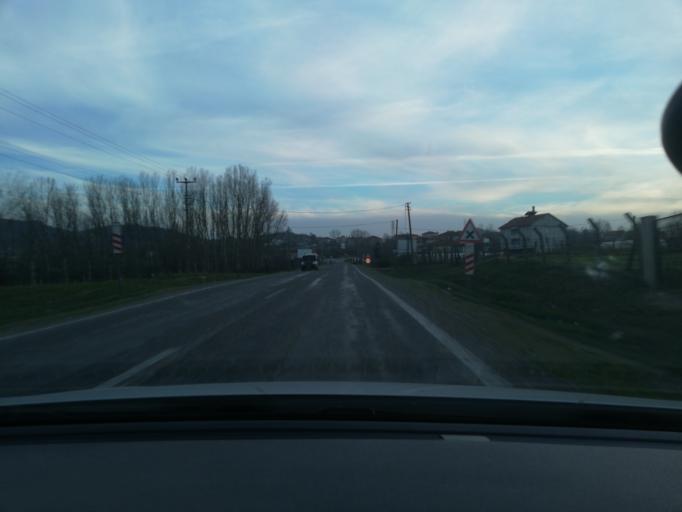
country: TR
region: Zonguldak
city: Saltukova
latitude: 41.5040
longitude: 32.0985
